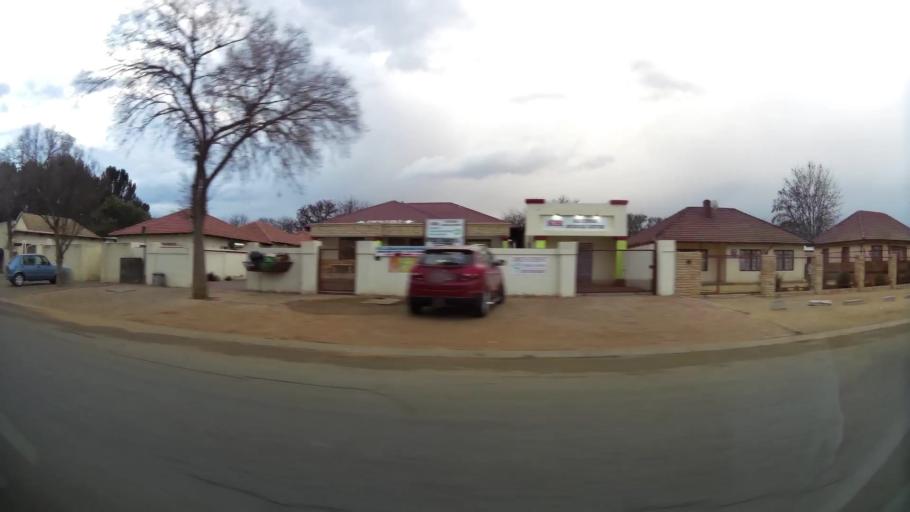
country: ZA
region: Orange Free State
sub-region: Lejweleputswa District Municipality
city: Welkom
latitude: -27.9751
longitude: 26.7716
